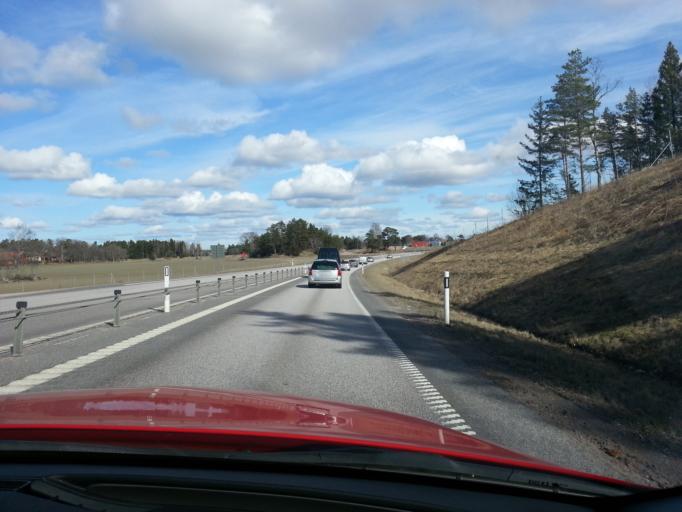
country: SE
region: Uppsala
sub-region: Uppsala Kommun
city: Storvreta
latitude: 59.9331
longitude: 17.8043
